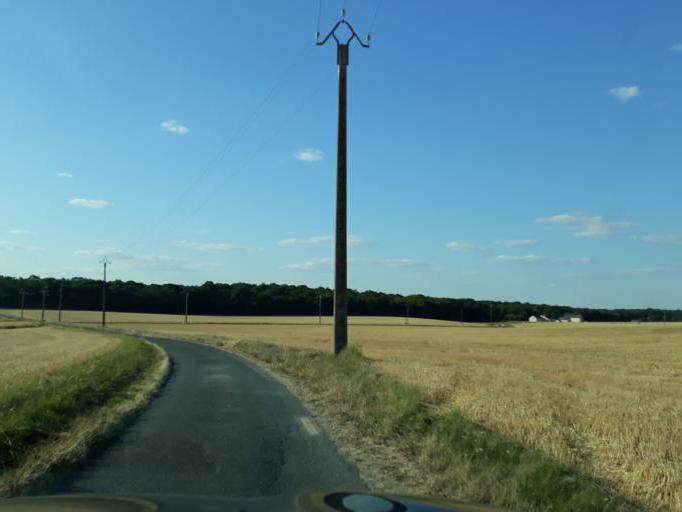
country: FR
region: Centre
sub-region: Departement du Loiret
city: Chaingy
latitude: 47.9047
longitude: 1.7585
